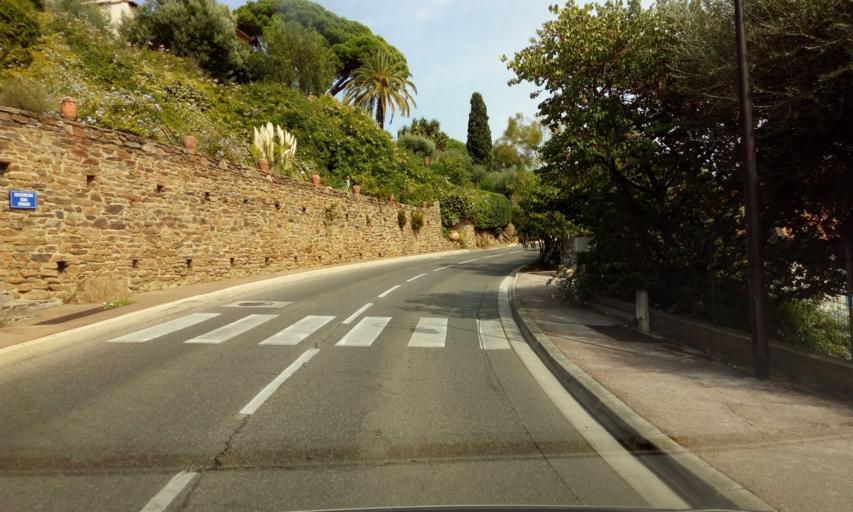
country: FR
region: Provence-Alpes-Cote d'Azur
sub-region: Departement du Var
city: Bormes-les-Mimosas
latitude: 43.1485
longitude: 6.3421
